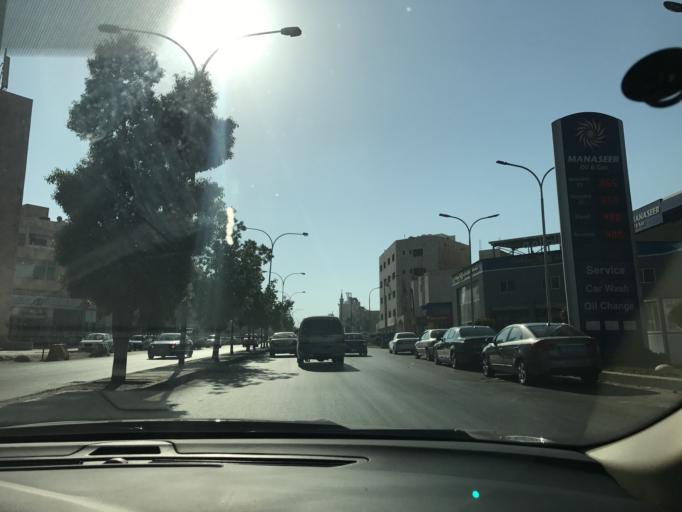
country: JO
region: Amman
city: Wadi as Sir
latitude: 31.9457
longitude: 35.8449
